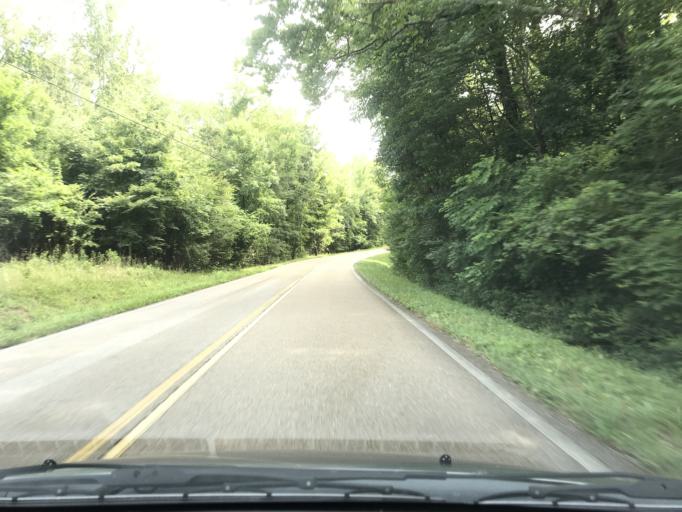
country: US
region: Tennessee
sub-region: Hamilton County
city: Lakesite
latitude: 35.1786
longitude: -85.1141
